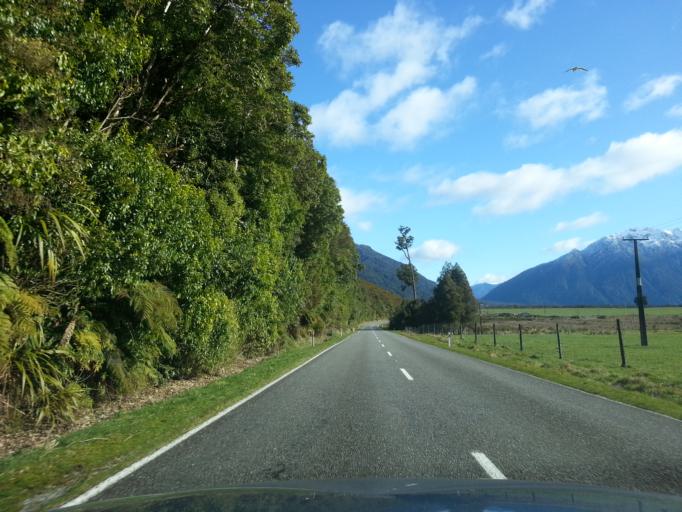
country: NZ
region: West Coast
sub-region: Grey District
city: Greymouth
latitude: -42.7448
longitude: 171.4204
